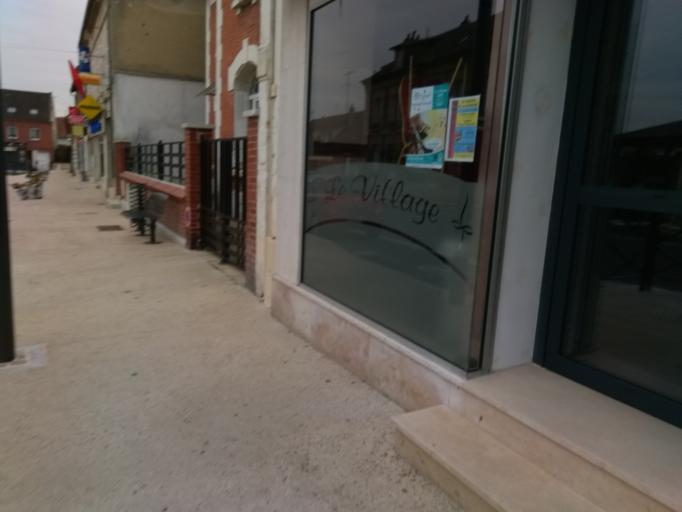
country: FR
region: Picardie
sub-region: Departement de l'Oise
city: Choisy-au-Bac
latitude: 49.4381
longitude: 2.8788
